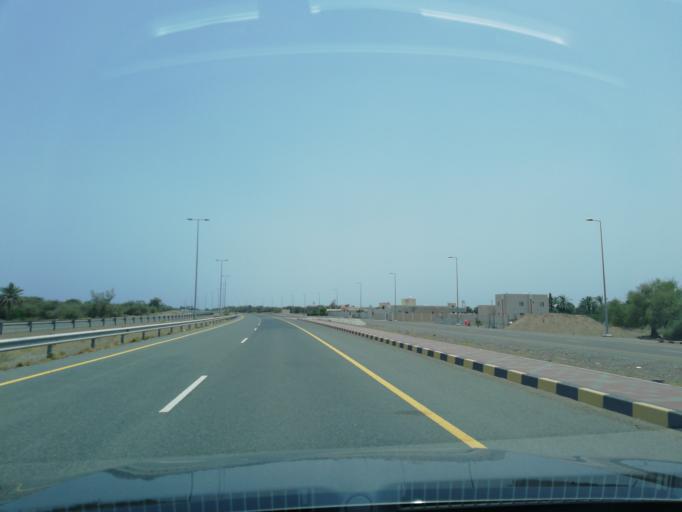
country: OM
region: Al Batinah
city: Shinas
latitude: 24.7937
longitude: 56.4524
